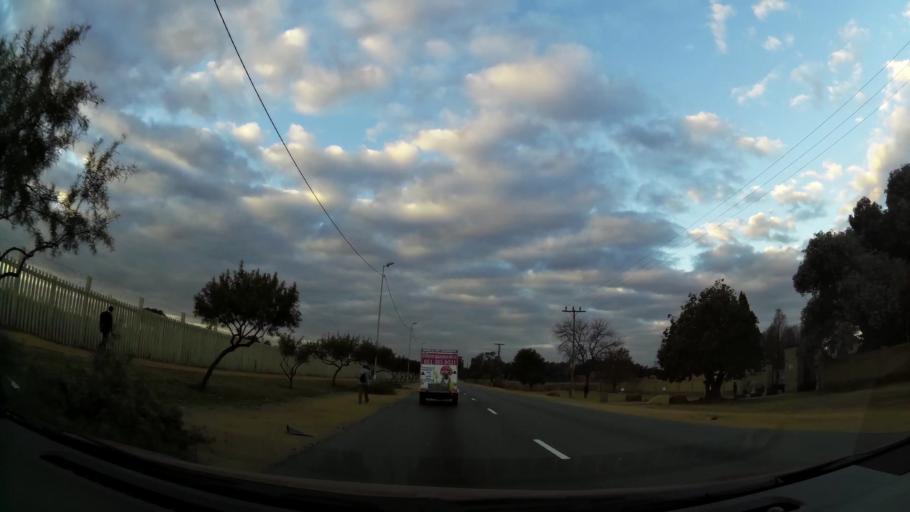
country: ZA
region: Gauteng
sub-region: City of Johannesburg Metropolitan Municipality
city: Midrand
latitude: -25.9922
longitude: 28.1491
